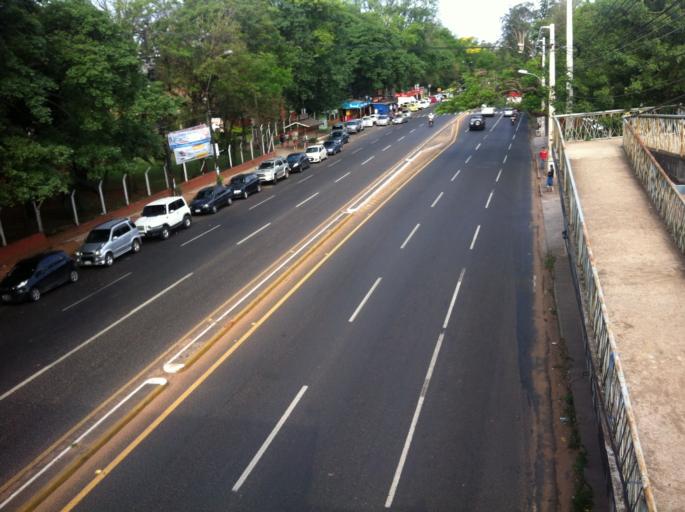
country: PY
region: Central
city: Fernando de la Mora
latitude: -25.3391
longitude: -57.5230
